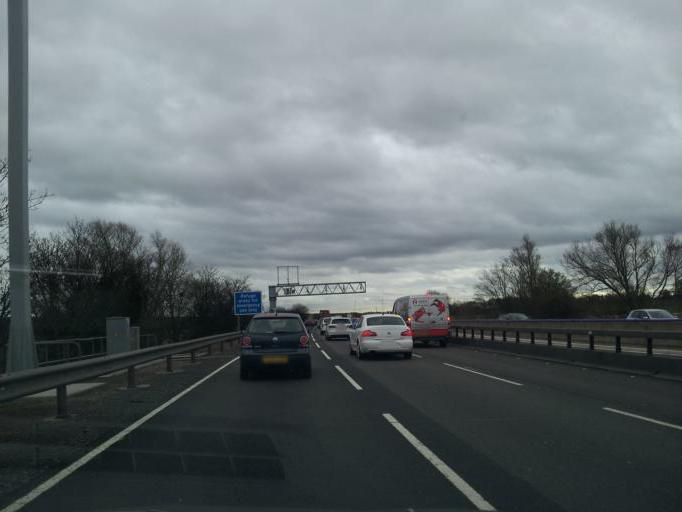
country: GB
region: England
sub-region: Staffordshire
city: Penkridge
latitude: 52.7588
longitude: -2.1026
